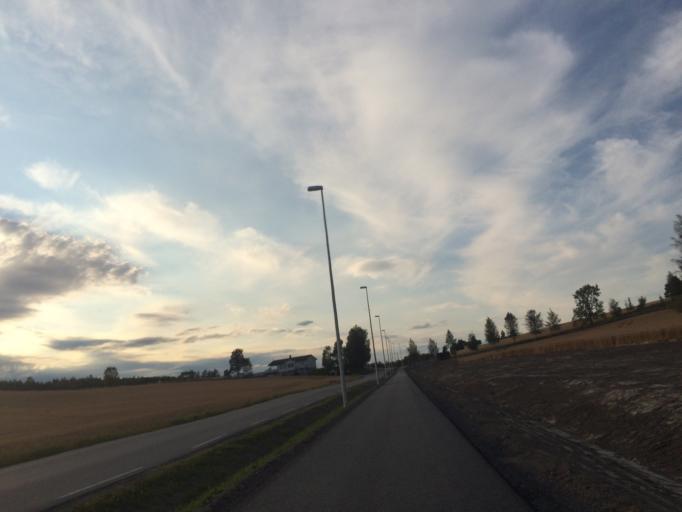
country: NO
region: Akershus
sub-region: Ski
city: Ski
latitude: 59.6879
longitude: 10.8665
